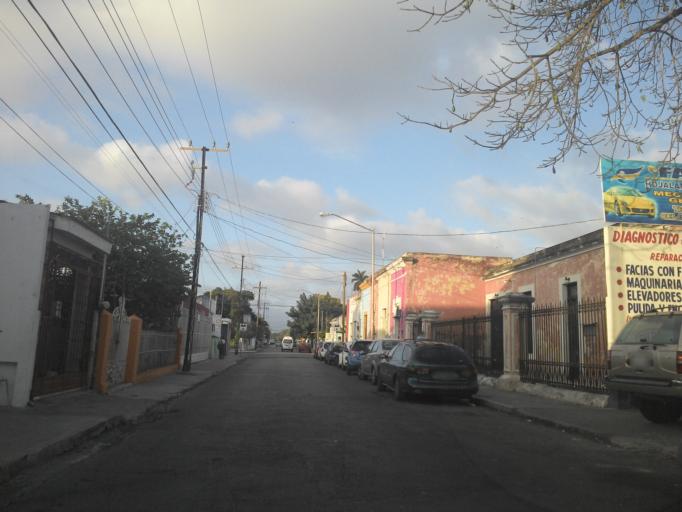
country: MX
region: Yucatan
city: Merida
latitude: 20.9748
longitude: -89.6287
